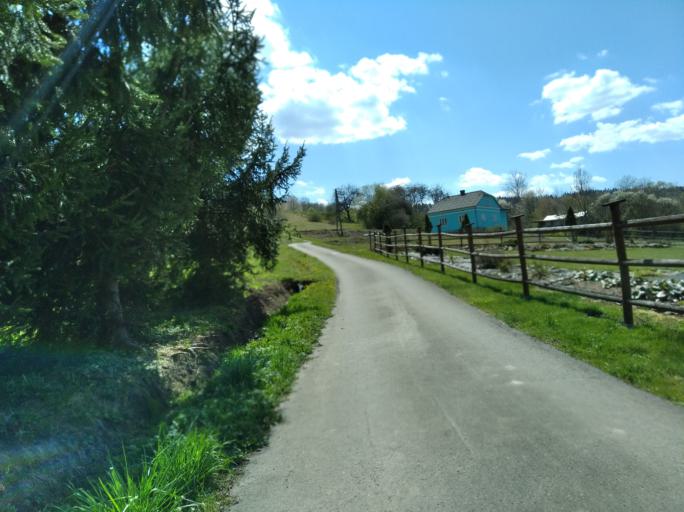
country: PL
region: Subcarpathian Voivodeship
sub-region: Powiat brzozowski
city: Blizne
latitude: 49.7851
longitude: 21.9850
